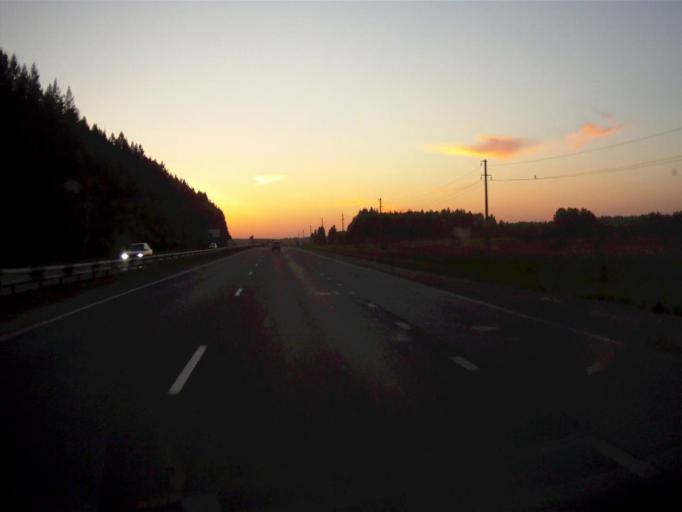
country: RU
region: Chelyabinsk
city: Roshchino
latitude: 55.1922
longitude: 61.2220
